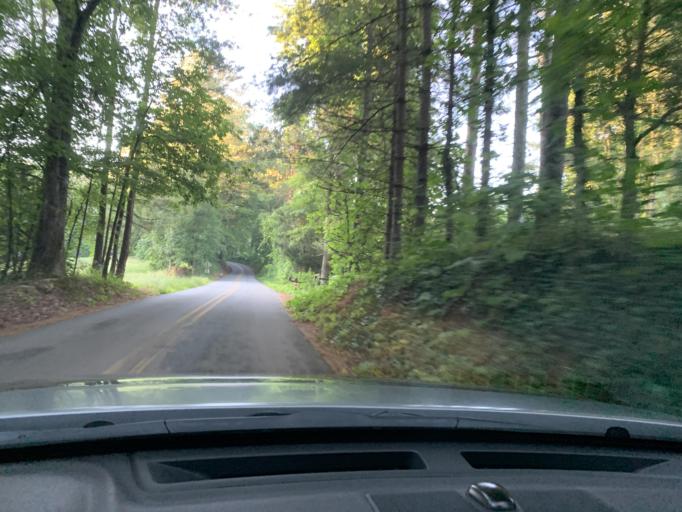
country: US
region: Georgia
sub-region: Bartow County
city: Rydal
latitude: 34.2289
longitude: -84.6558
